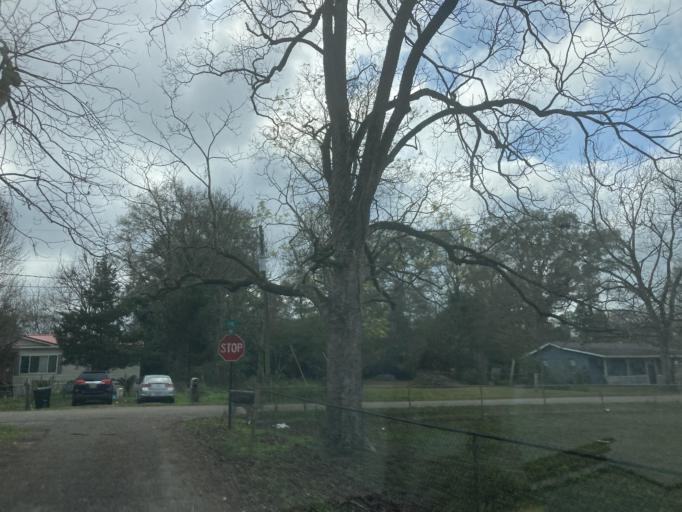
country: US
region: Mississippi
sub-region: Stone County
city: Wiggins
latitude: 30.8944
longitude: -89.1626
